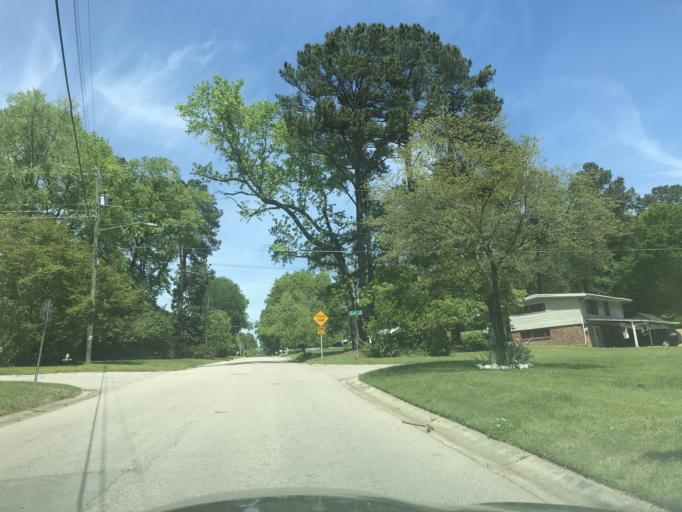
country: US
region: North Carolina
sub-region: Wake County
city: Raleigh
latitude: 35.8271
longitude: -78.5809
